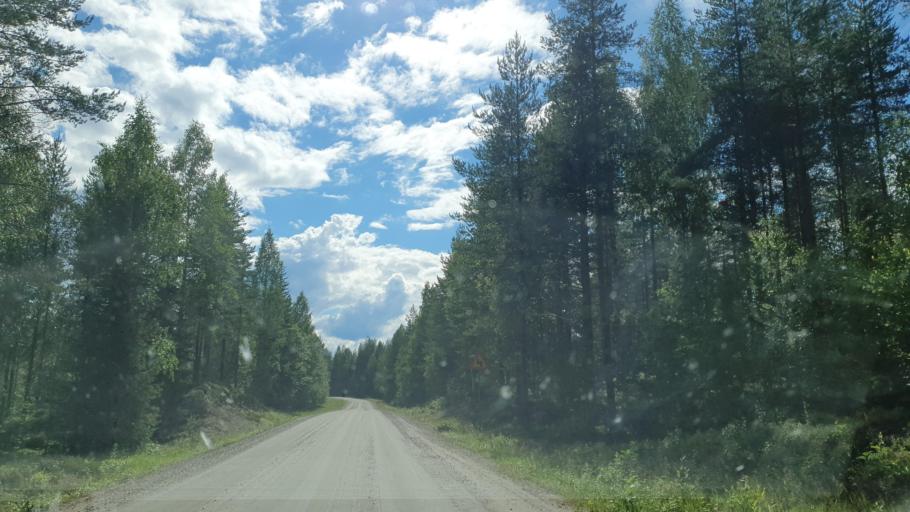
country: FI
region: Kainuu
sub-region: Kehys-Kainuu
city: Kuhmo
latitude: 64.1444
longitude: 29.7067
